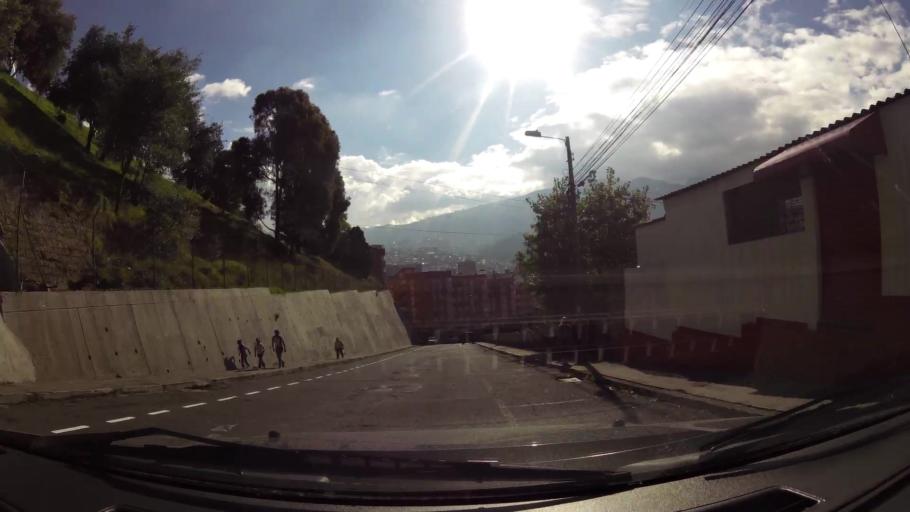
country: EC
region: Pichincha
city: Quito
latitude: -0.2136
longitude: -78.4943
